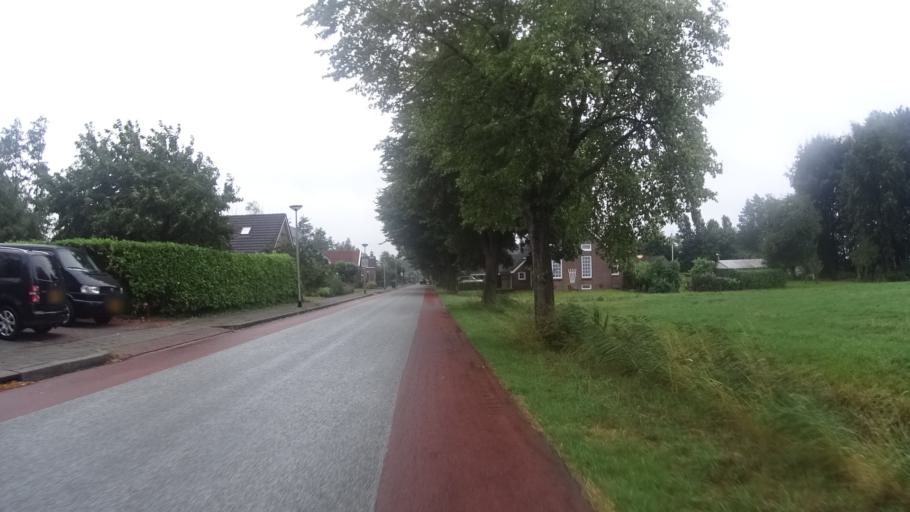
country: NL
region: Groningen
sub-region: Gemeente  Oldambt
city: Winschoten
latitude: 53.1815
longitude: 6.9544
